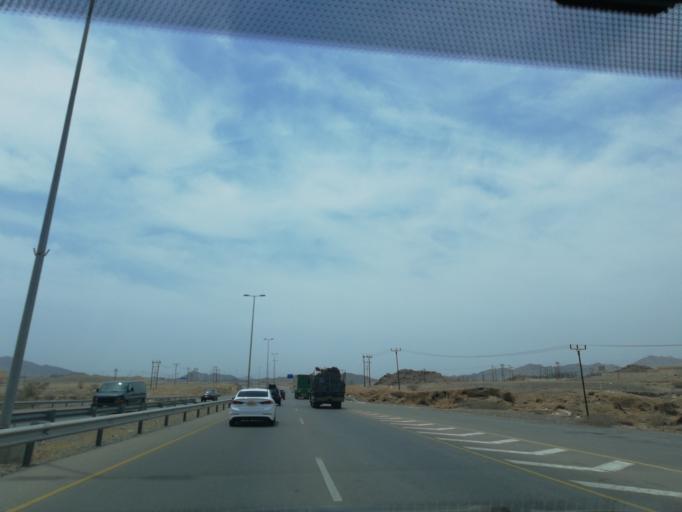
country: OM
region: Muhafazat ad Dakhiliyah
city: Bidbid
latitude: 23.4438
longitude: 58.1219
